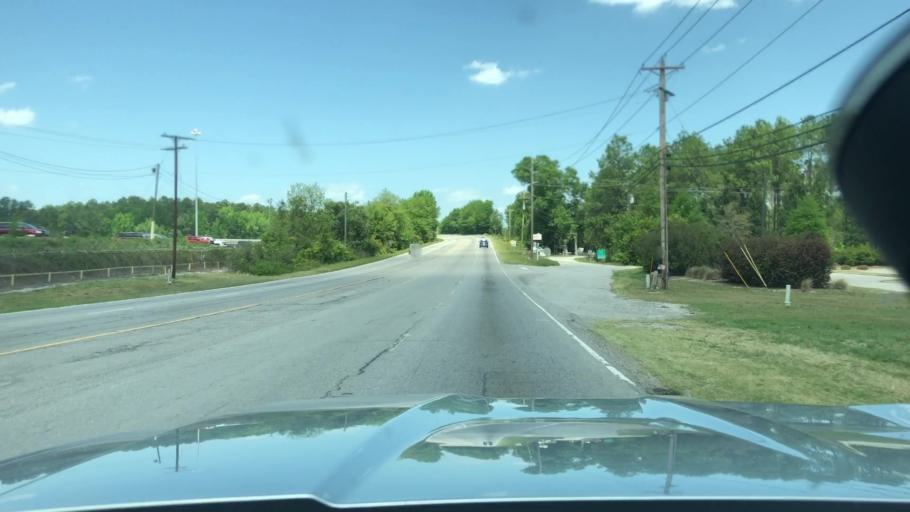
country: US
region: South Carolina
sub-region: Lexington County
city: Pineridge
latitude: 33.9049
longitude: -81.0654
